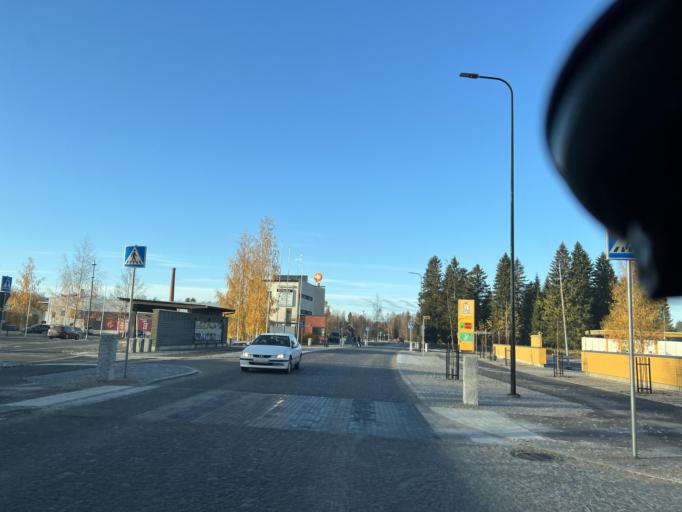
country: FI
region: Northern Ostrobothnia
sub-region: Oulu
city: Tyrnaevae
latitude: 64.7631
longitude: 25.6491
